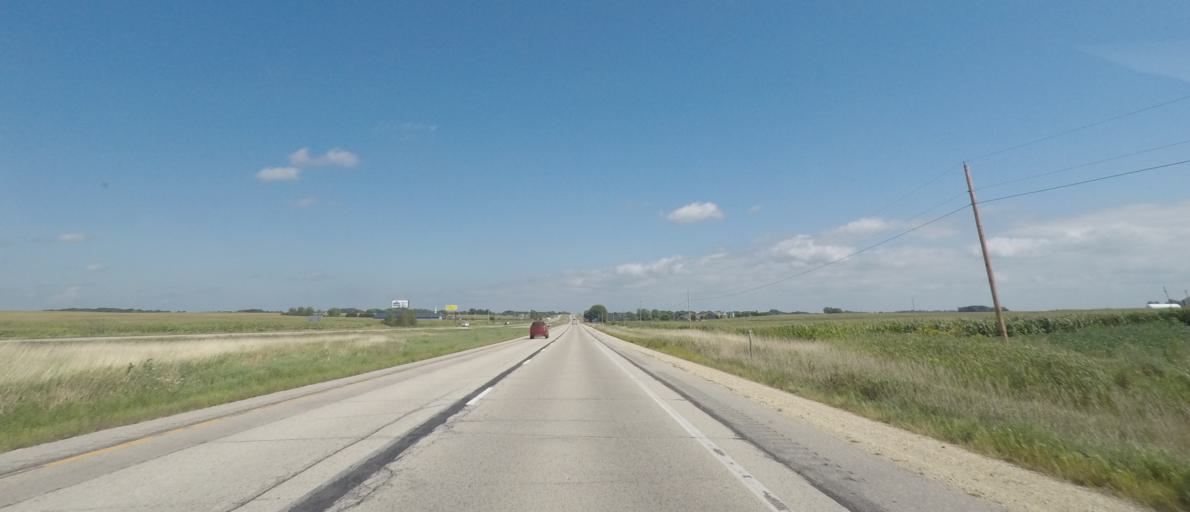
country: US
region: Iowa
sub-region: Jones County
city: Anamosa
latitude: 42.0707
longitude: -91.3560
